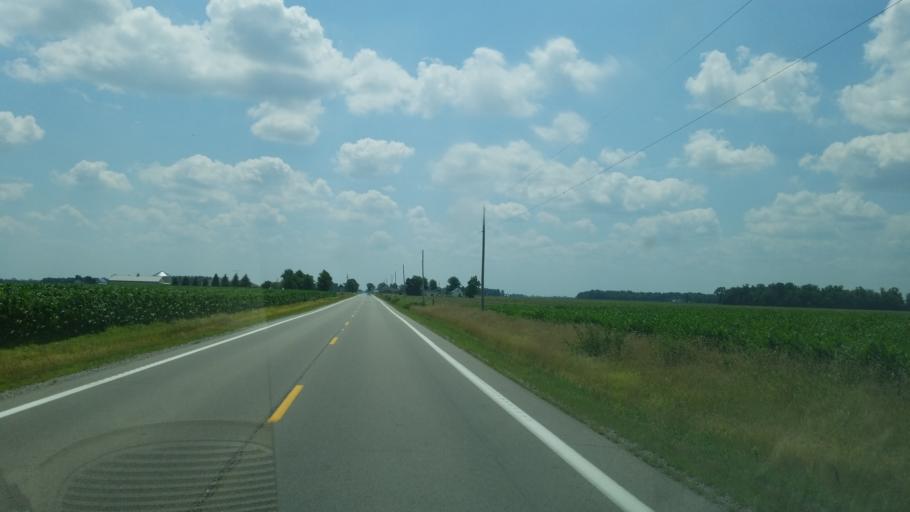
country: US
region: Ohio
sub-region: Henry County
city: Deshler
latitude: 41.2651
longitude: -83.9404
